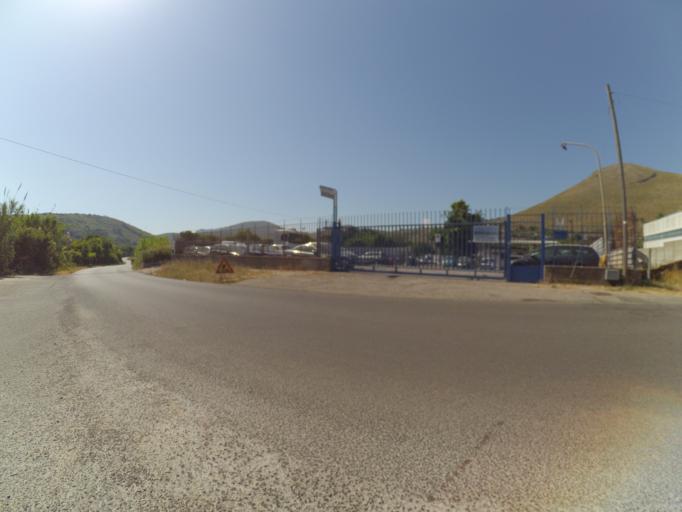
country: IT
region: Latium
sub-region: Provincia di Latina
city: Gaeta
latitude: 41.2298
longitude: 13.5340
